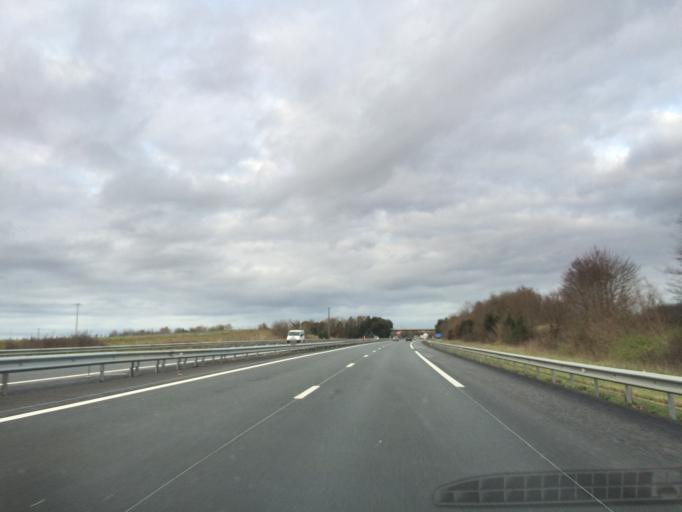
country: FR
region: Poitou-Charentes
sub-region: Departement des Deux-Sevres
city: Aiffres
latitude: 46.2828
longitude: -0.3970
